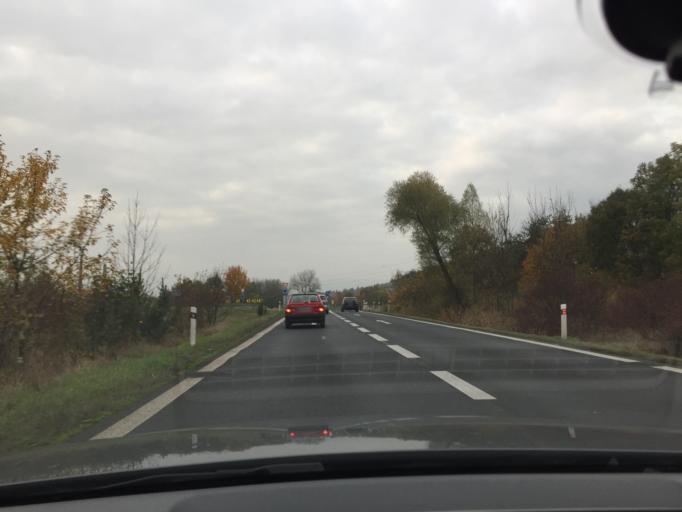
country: CZ
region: Ustecky
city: Bystrany
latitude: 50.6236
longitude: 13.8721
